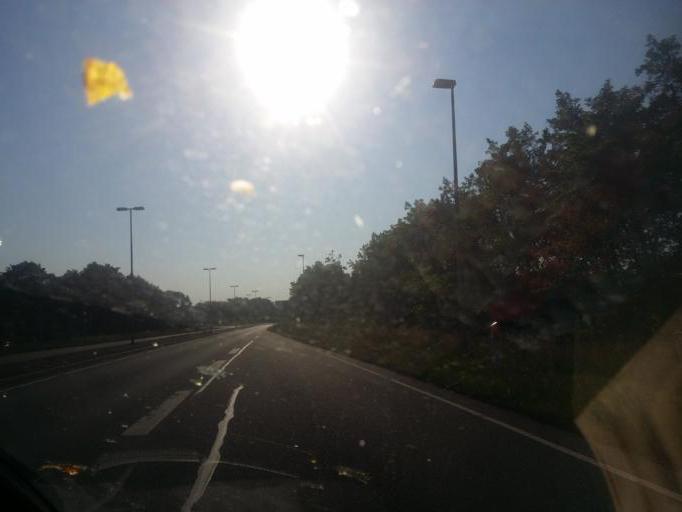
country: DK
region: South Denmark
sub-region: Esbjerg Kommune
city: Ribe
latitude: 55.3208
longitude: 8.7572
